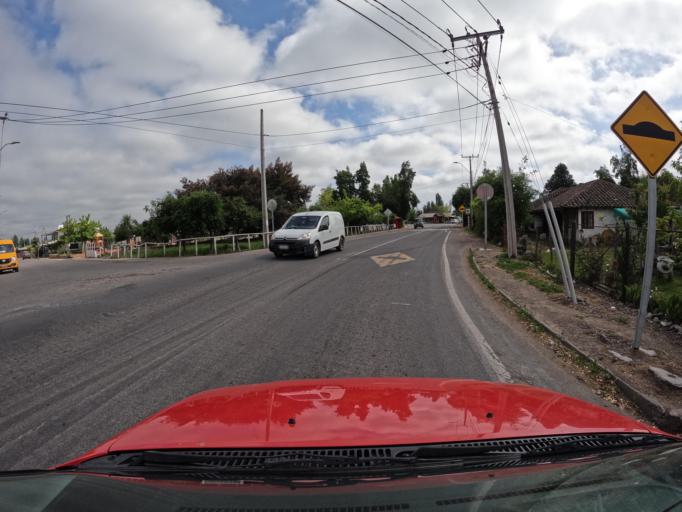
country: CL
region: O'Higgins
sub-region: Provincia de Colchagua
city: Santa Cruz
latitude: -34.6933
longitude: -71.3171
